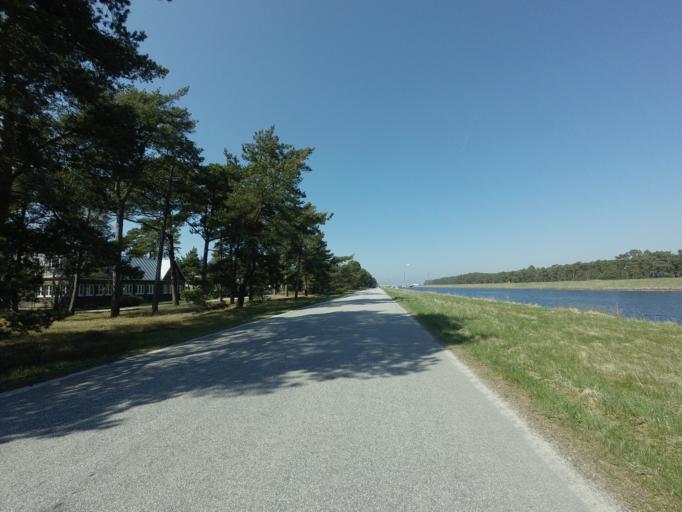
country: SE
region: Skane
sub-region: Vellinge Kommun
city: Ljunghusen
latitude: 55.4030
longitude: 12.9398
